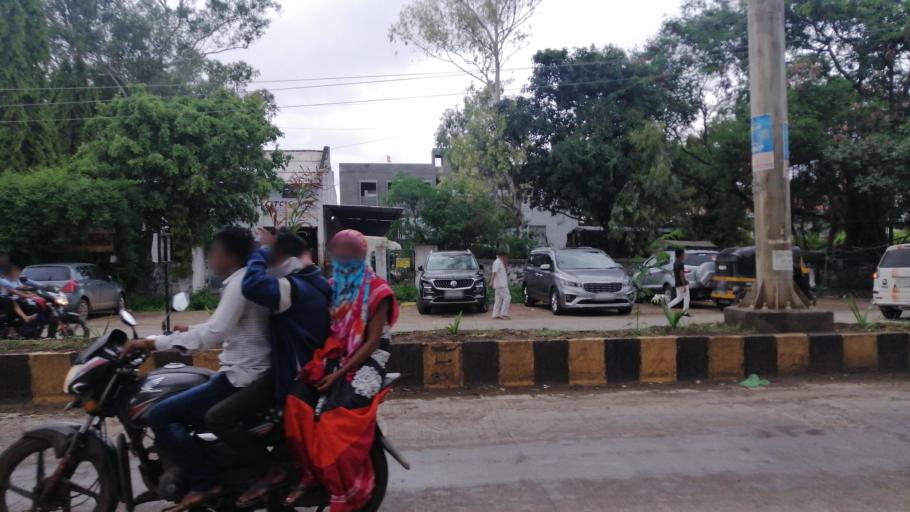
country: IN
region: Maharashtra
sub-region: Aurangabad Division
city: Aurangabad
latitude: 19.8781
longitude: 75.3713
